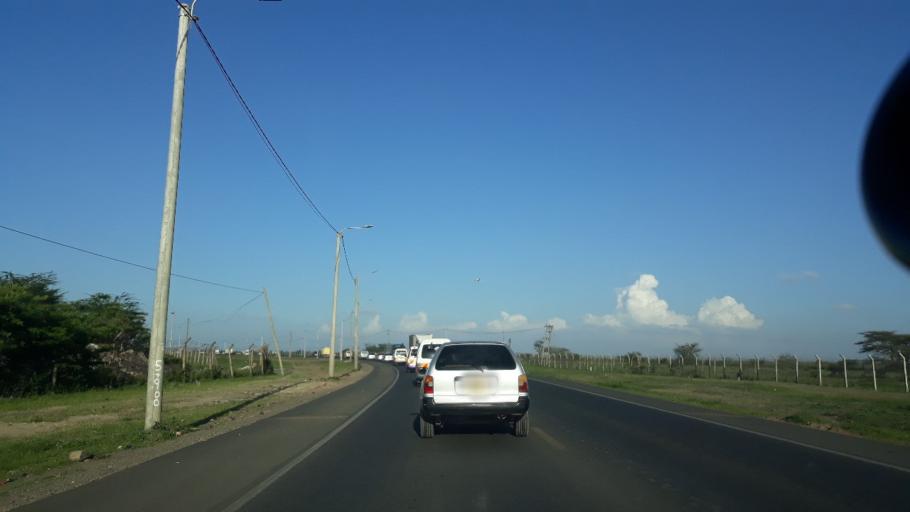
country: KE
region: Nairobi Area
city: Pumwani
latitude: -1.3108
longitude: 36.9290
